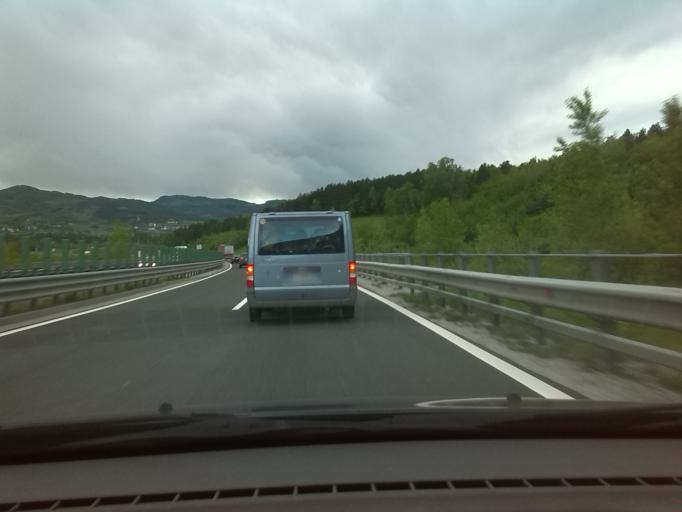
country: SI
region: Vipava
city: Vipava
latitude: 45.8109
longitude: 13.9756
